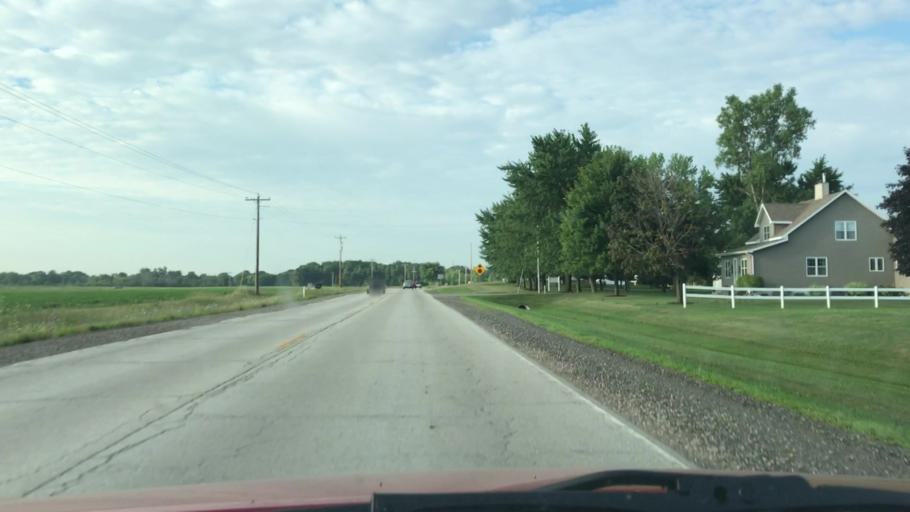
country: US
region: Wisconsin
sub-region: Brown County
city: De Pere
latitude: 44.4338
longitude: -88.1359
